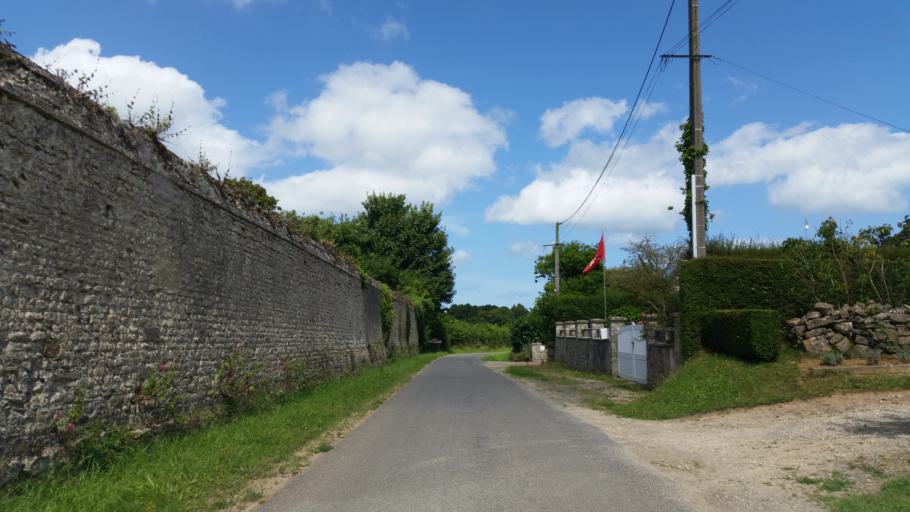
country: FR
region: Lower Normandy
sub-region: Departement de la Manche
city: Montebourg
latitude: 49.4603
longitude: -1.3412
